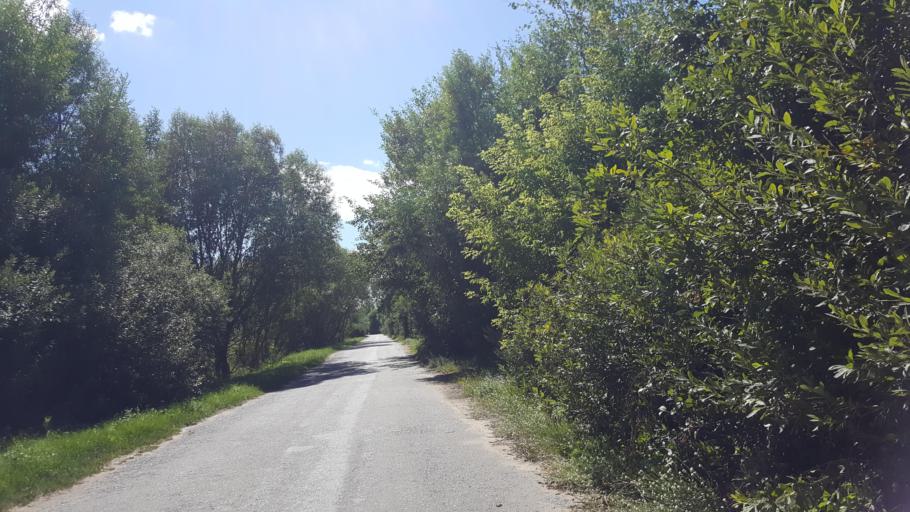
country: BY
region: Brest
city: Kobryn
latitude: 52.3155
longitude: 24.2999
